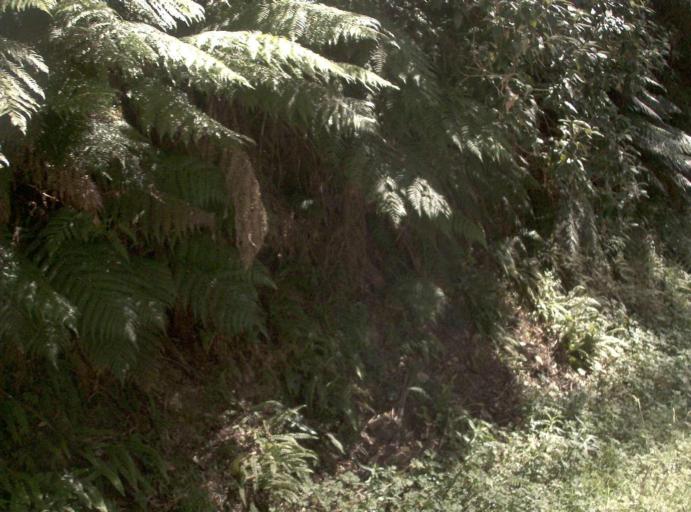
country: AU
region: Victoria
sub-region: Yarra Ranges
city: Millgrove
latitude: -37.7273
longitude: 145.6999
